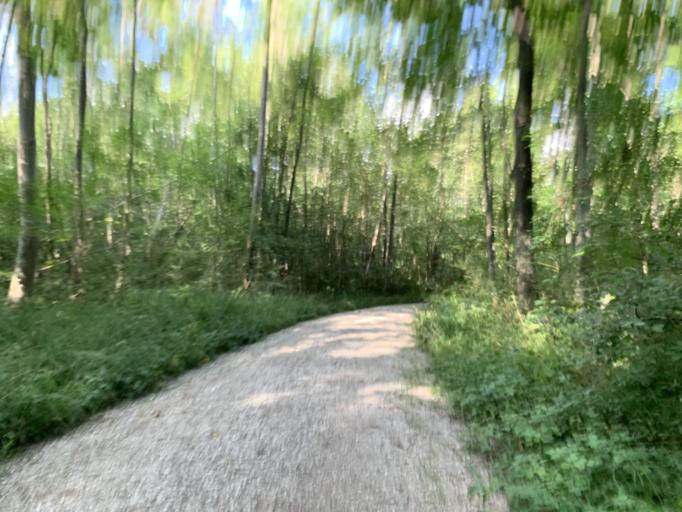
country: DE
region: Bavaria
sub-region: Upper Bavaria
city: Freising
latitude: 48.4028
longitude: 11.7684
